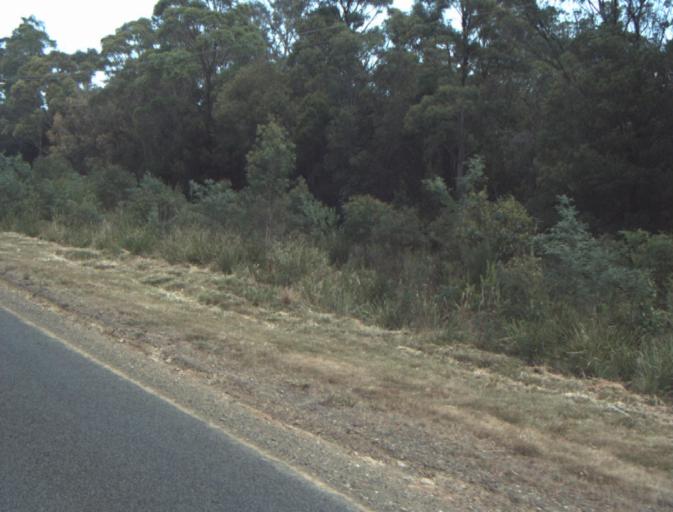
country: AU
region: Tasmania
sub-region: Launceston
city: Mayfield
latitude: -41.3138
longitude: 147.1350
